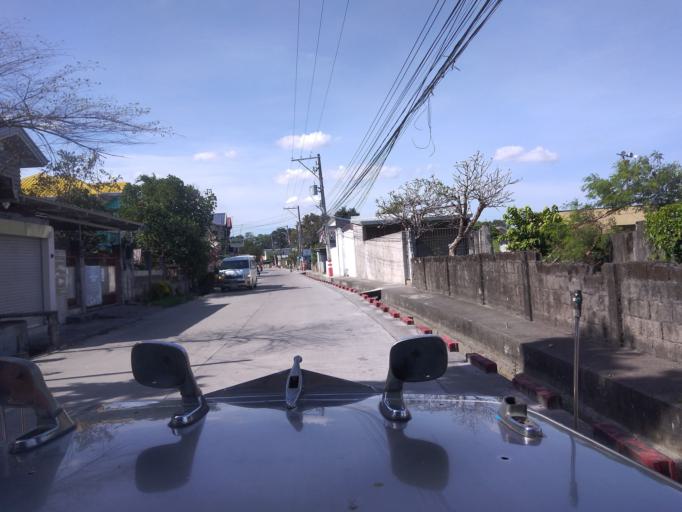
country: PH
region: Central Luzon
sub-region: Province of Pampanga
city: Magliman
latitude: 15.0336
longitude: 120.6663
